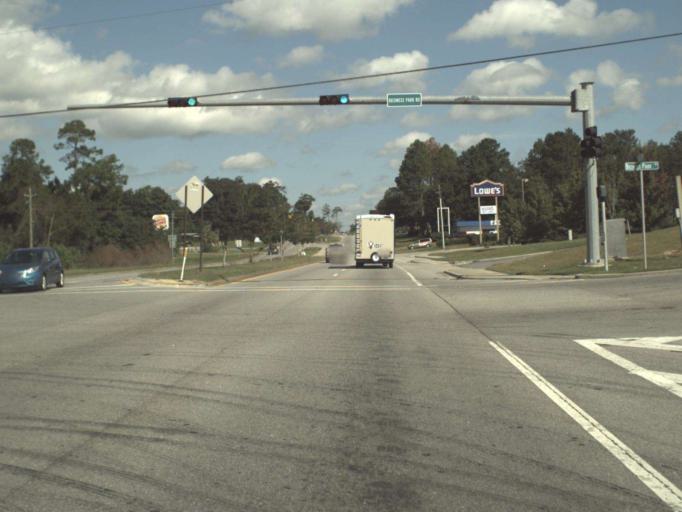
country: US
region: Florida
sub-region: Walton County
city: DeFuniak Springs
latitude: 30.6964
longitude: -86.1224
